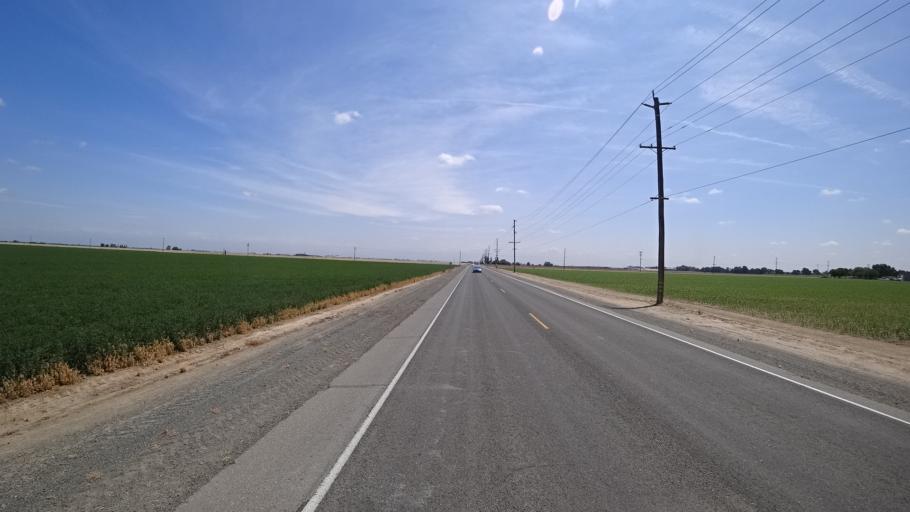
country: US
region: California
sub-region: Tulare County
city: Goshen
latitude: 36.2981
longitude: -119.4752
